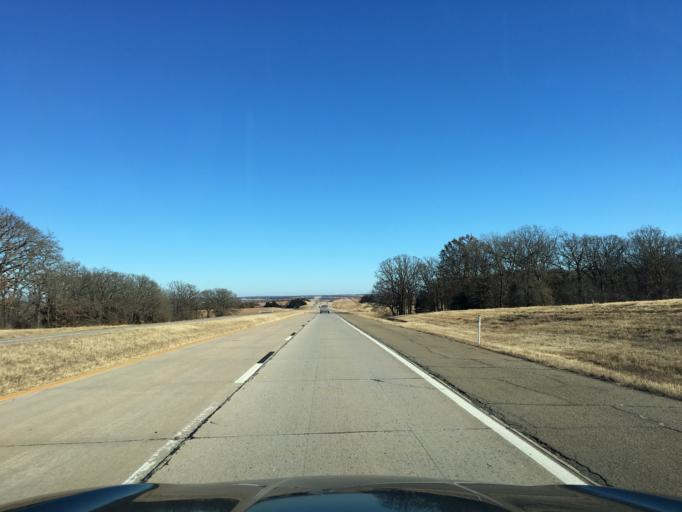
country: US
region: Oklahoma
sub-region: Payne County
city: Yale
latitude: 36.2240
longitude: -96.7460
